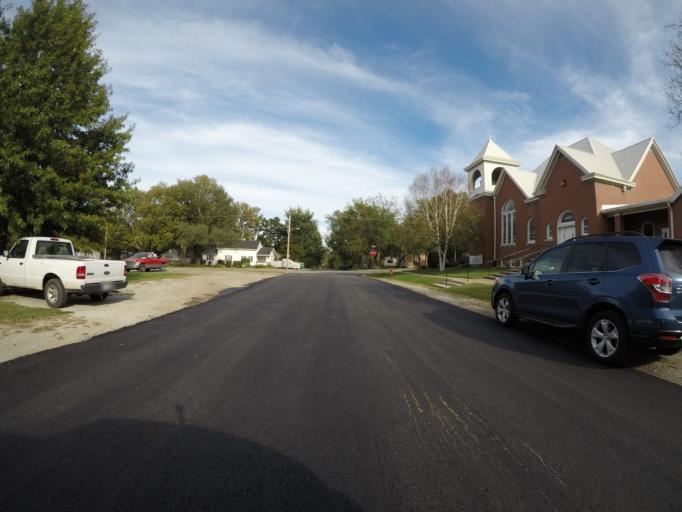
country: US
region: Kansas
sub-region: Johnson County
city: Edgerton
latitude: 38.7658
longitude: -95.0075
